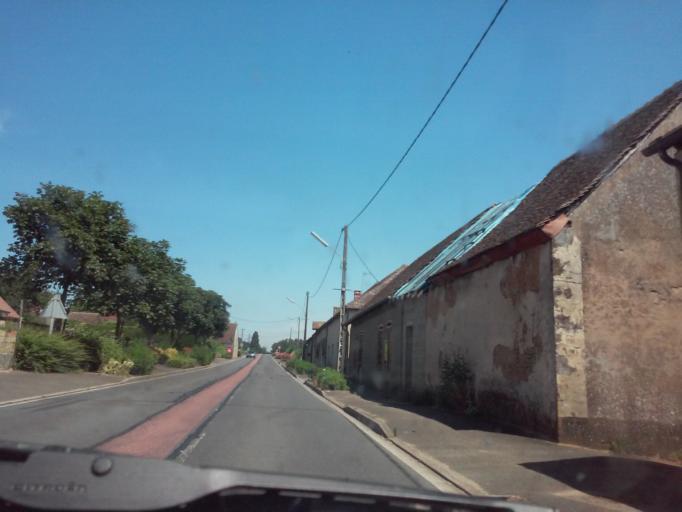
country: FR
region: Pays de la Loire
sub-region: Departement de la Sarthe
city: Beaufay
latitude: 48.1104
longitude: 0.3385
